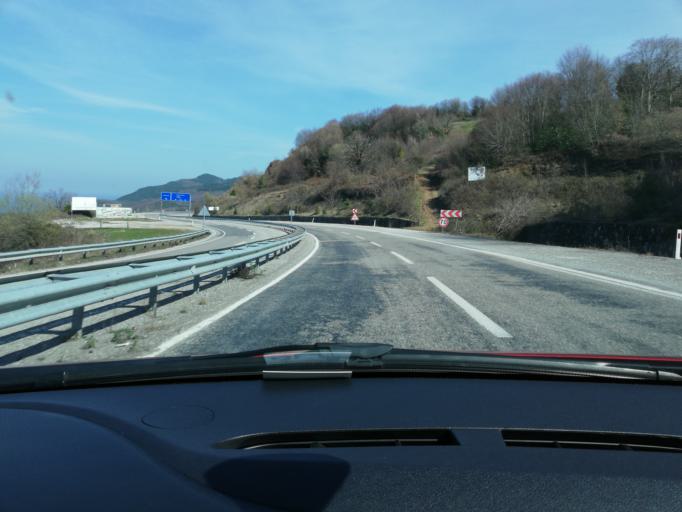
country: TR
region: Bartin
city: Amasra
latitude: 41.7378
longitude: 32.4263
